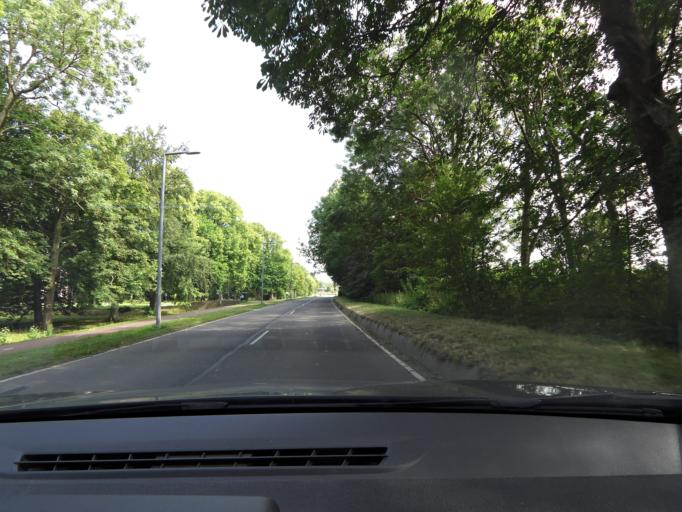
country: NL
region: South Holland
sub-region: Gemeente Schiedam
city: Schiedam
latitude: 51.9532
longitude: 4.4056
